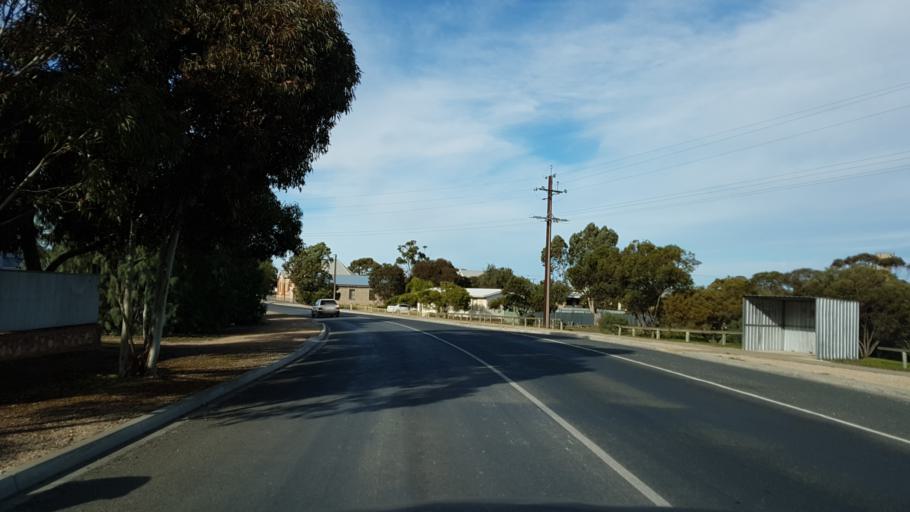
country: AU
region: South Australia
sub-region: Murray Bridge
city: Tailem Bend
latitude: -35.2499
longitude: 139.4552
